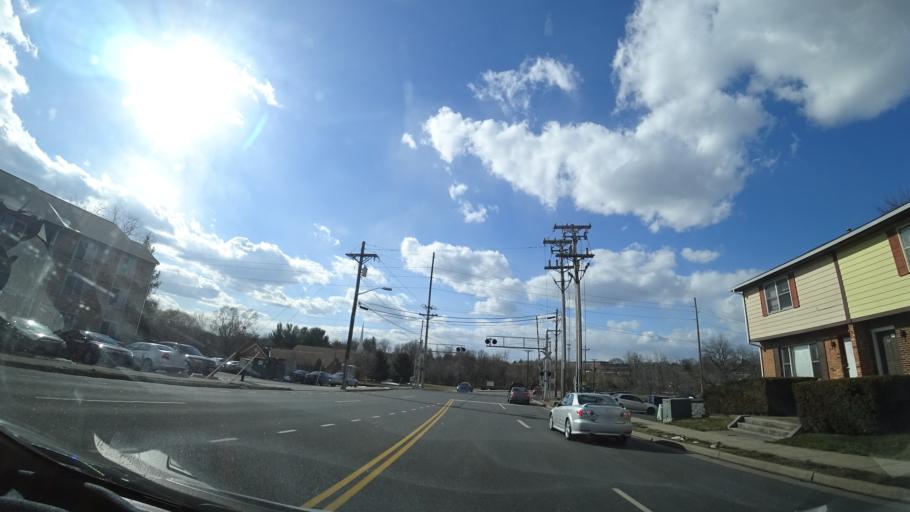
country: US
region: Virginia
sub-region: City of Harrisonburg
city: Harrisonburg
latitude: 38.4363
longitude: -78.8804
